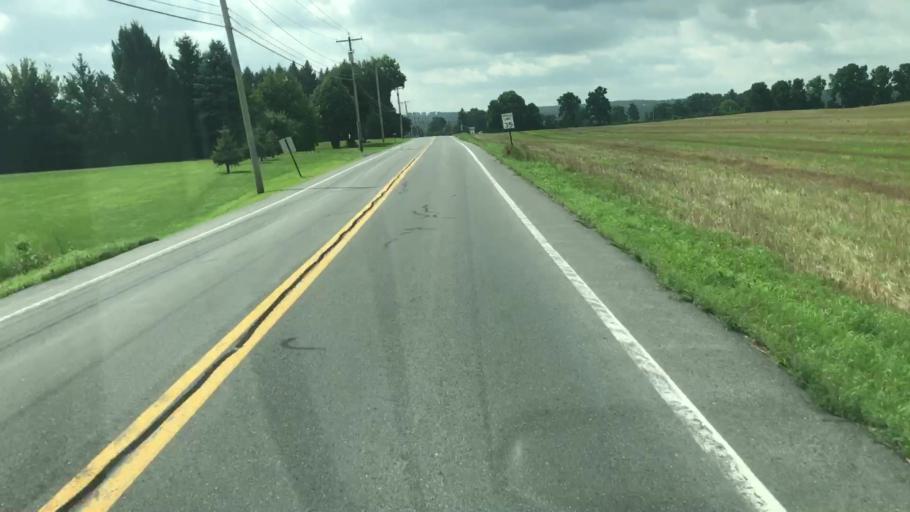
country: US
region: New York
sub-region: Onondaga County
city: Peru
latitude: 43.0399
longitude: -76.3657
